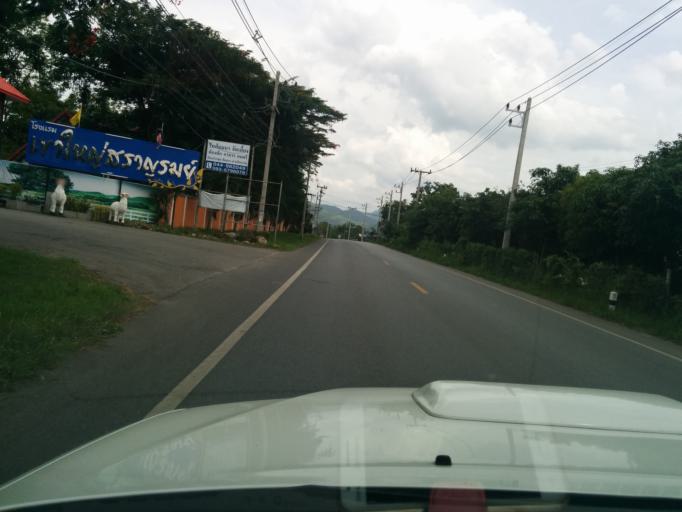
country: TH
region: Sara Buri
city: Muak Lek
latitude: 14.6109
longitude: 101.2123
